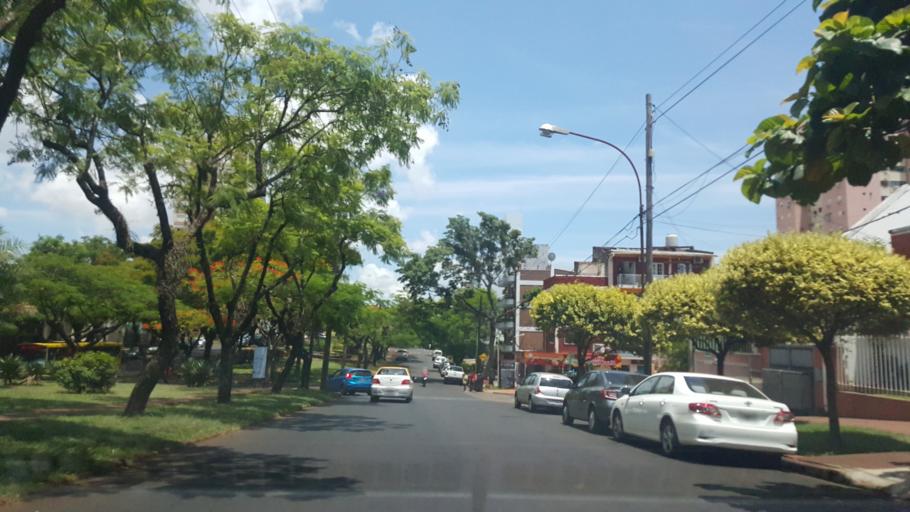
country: AR
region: Misiones
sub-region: Departamento de Capital
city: Posadas
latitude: -27.3607
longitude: -55.8964
